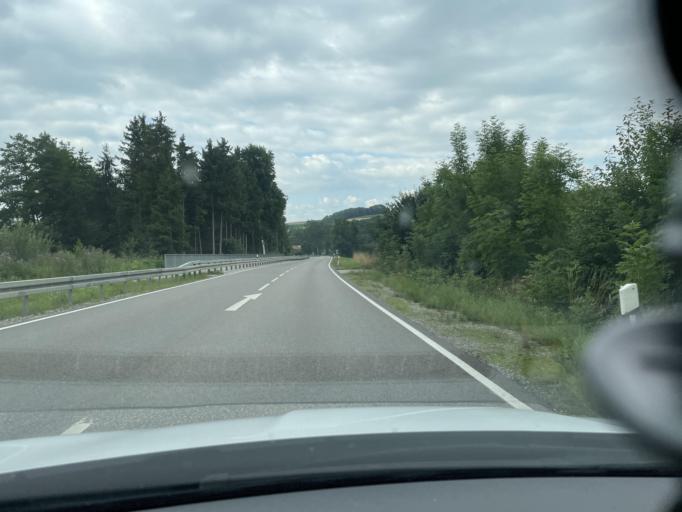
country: DE
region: Bavaria
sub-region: Upper Bavaria
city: Sankt Wolfgang
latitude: 48.1991
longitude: 12.1456
